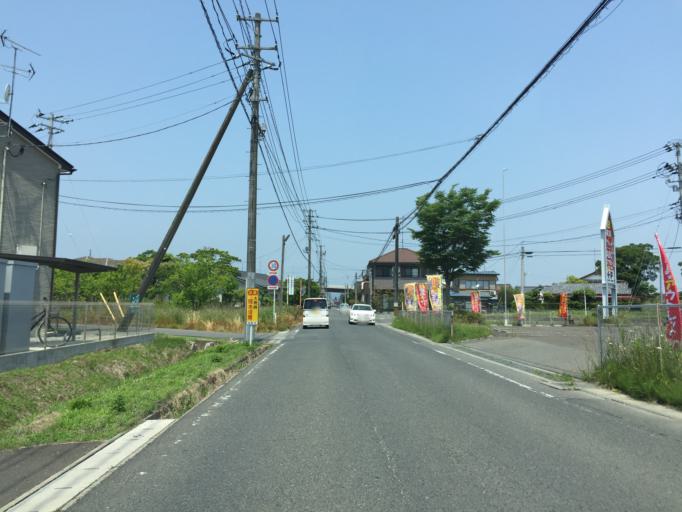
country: JP
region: Miyagi
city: Marumori
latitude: 37.7891
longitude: 140.9279
